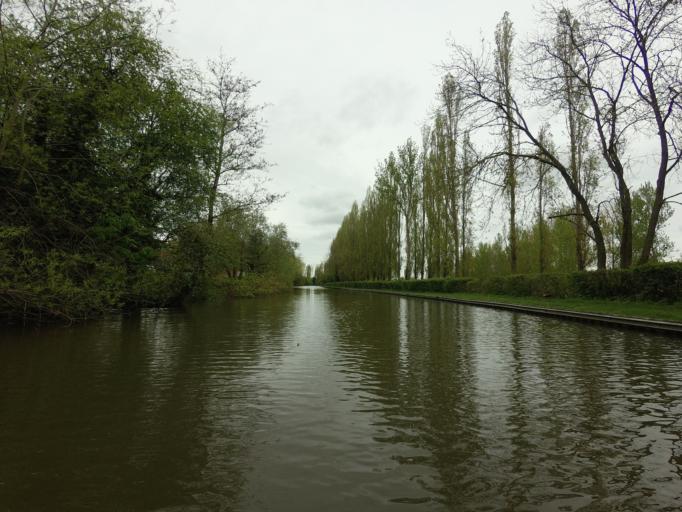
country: GB
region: England
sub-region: Milton Keynes
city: Milton Keynes
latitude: 52.0322
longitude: -0.7315
